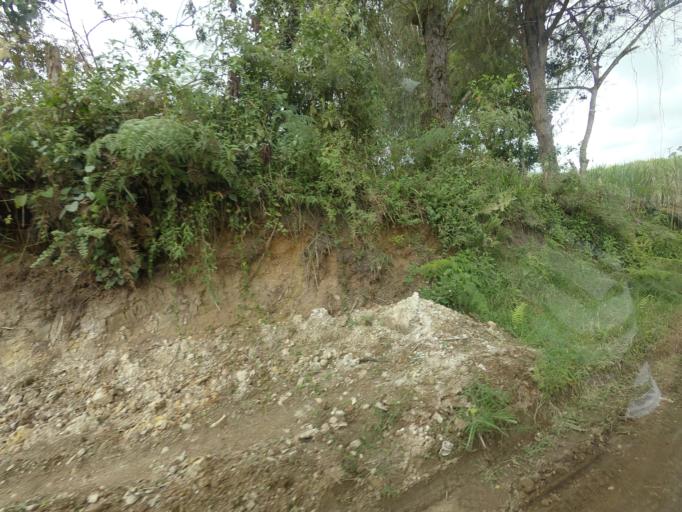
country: CO
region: Huila
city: San Agustin
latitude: 1.9425
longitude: -76.2988
